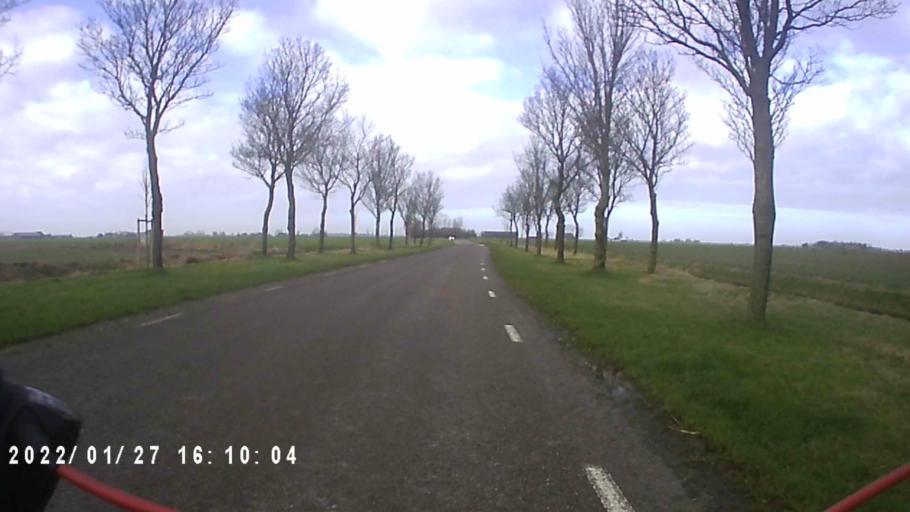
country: NL
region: Friesland
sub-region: Gemeente Dongeradeel
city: Anjum
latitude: 53.3812
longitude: 6.0816
